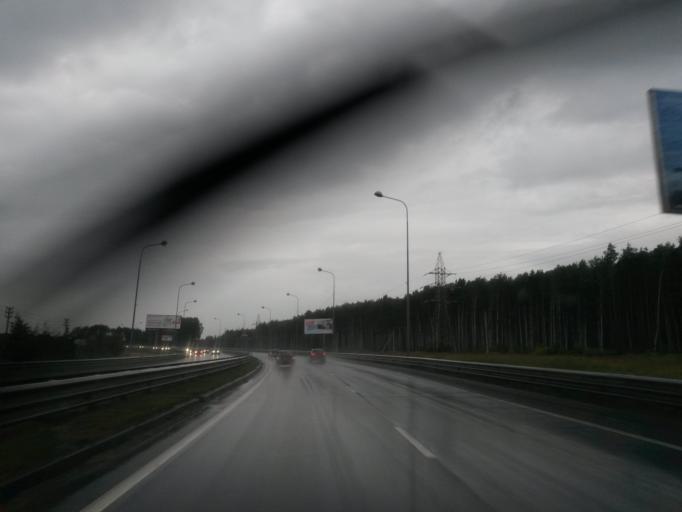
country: RU
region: Jaroslavl
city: Yaroslavl
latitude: 57.6834
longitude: 39.8854
